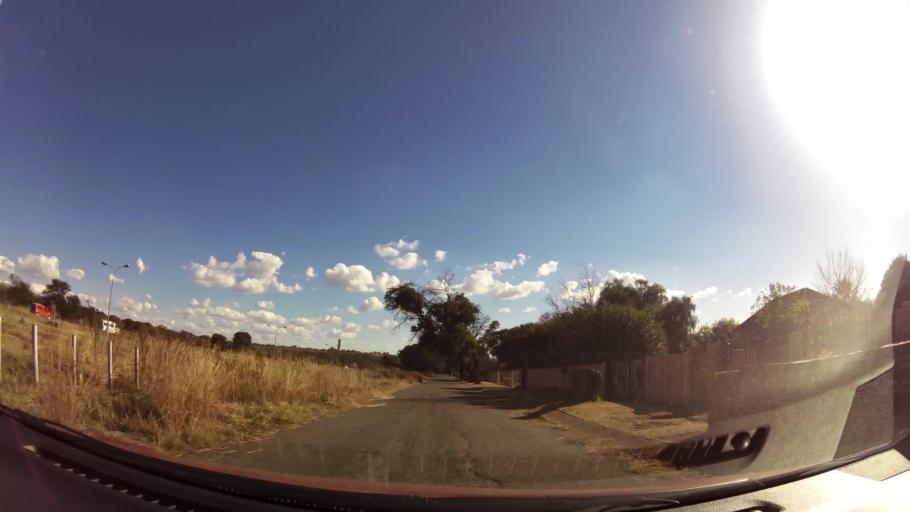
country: ZA
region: Gauteng
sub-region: West Rand District Municipality
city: Carletonville
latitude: -26.3747
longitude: 27.4031
